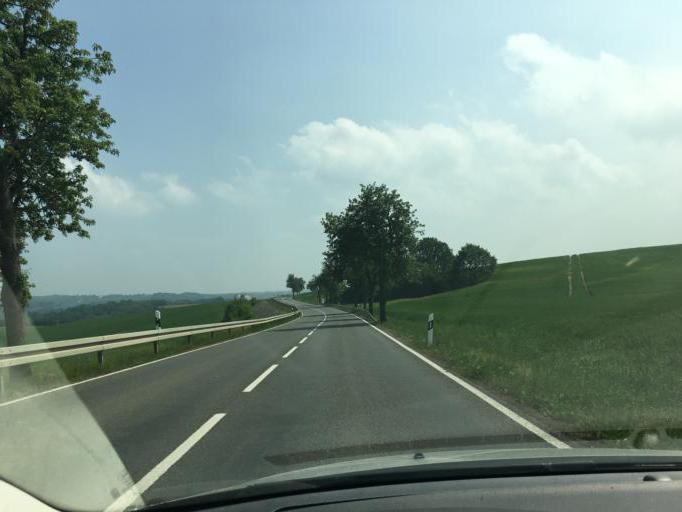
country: DE
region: Saxony
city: Colditz
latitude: 51.1474
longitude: 12.7674
